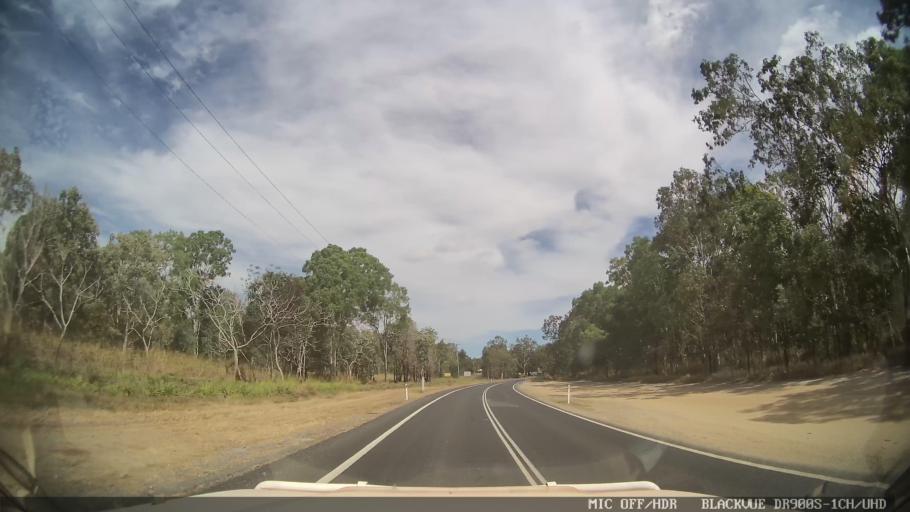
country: AU
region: Queensland
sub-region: Cairns
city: Port Douglas
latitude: -16.6680
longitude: 145.3291
